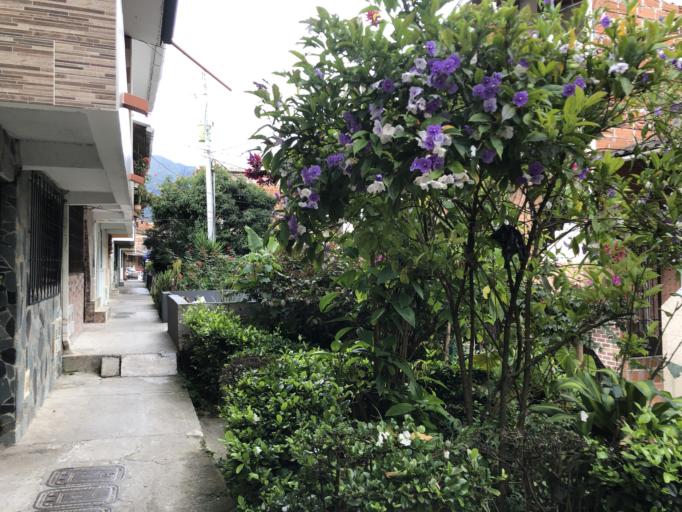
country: CO
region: Antioquia
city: Municipio de Copacabana
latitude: 6.3460
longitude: -75.5323
